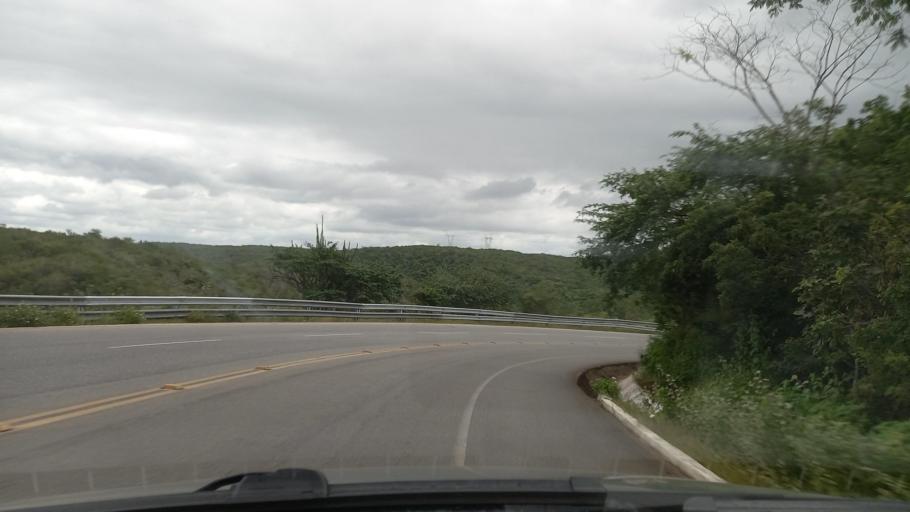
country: BR
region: Sergipe
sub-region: Caninde De Sao Francisco
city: Caninde de Sao Francisco
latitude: -9.6505
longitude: -37.7957
